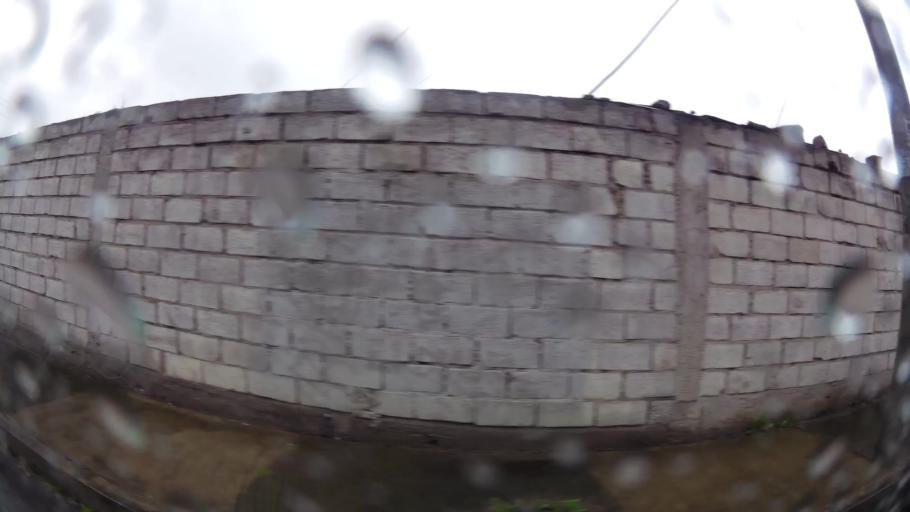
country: EC
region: Pichincha
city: Quito
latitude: -0.1016
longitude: -78.5020
